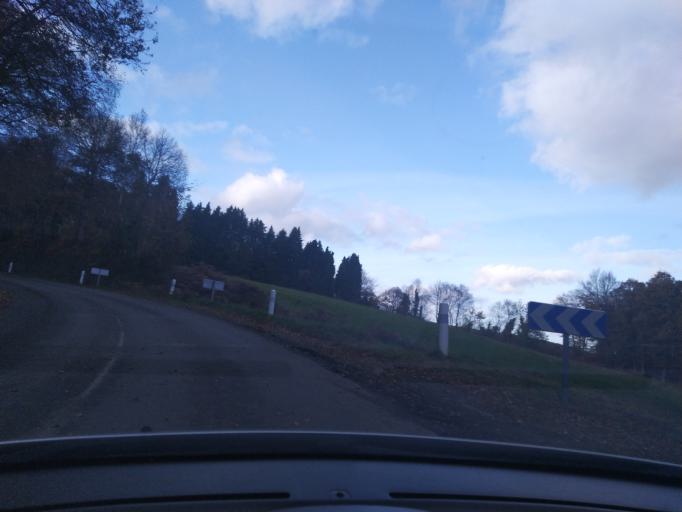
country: FR
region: Brittany
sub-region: Departement du Finistere
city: Plouigneau
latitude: 48.5708
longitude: -3.6459
